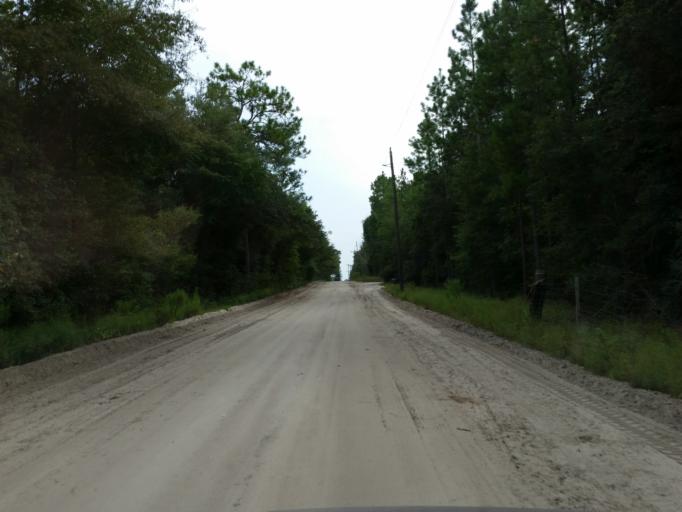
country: US
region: Florida
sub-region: Madison County
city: Madison
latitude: 30.5140
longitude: -83.2200
